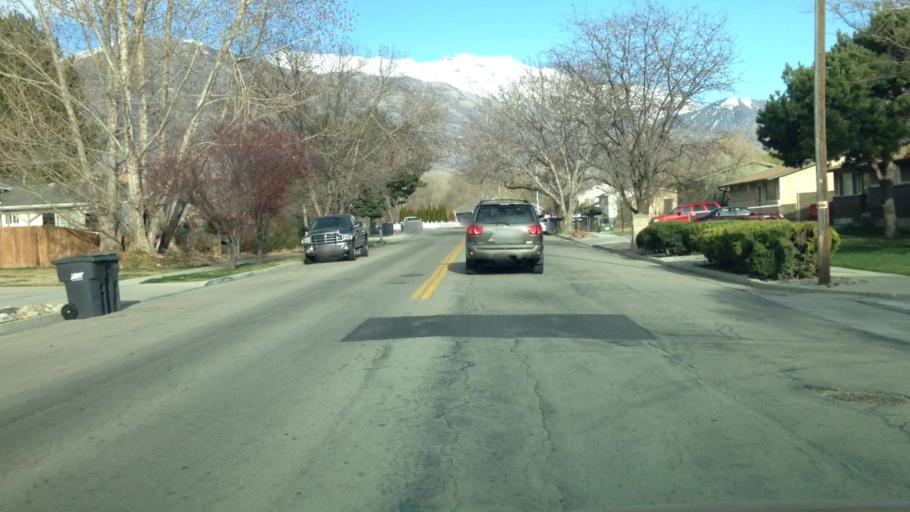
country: US
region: Utah
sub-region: Utah County
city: American Fork
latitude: 40.3910
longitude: -111.7890
